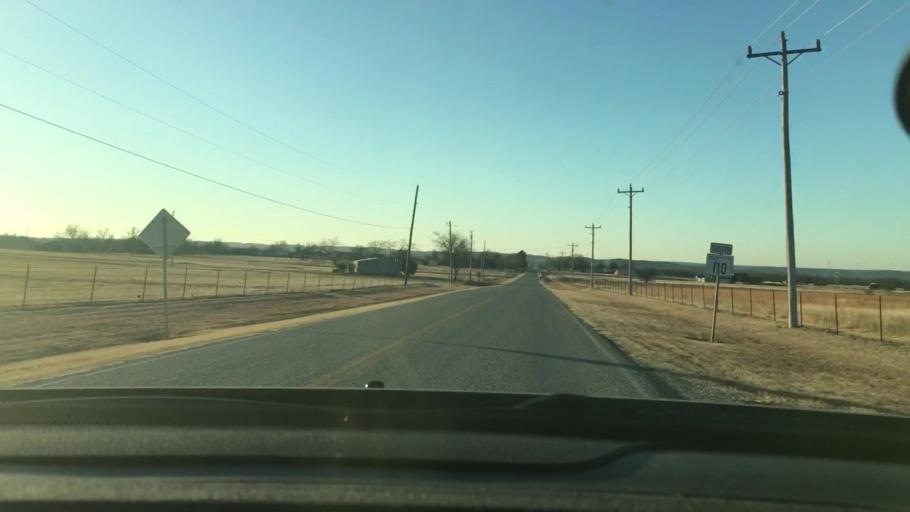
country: US
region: Oklahoma
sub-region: Murray County
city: Davis
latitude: 34.5040
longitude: -97.0903
